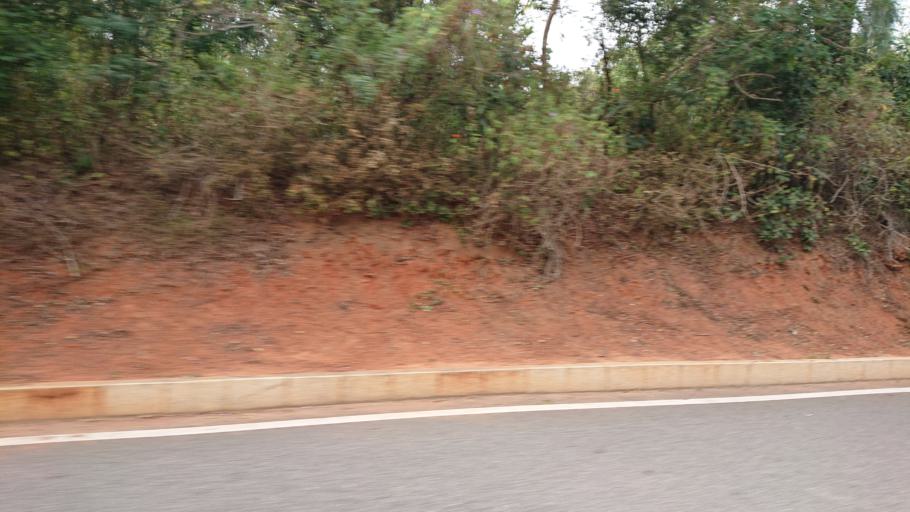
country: TW
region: Fukien
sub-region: Kinmen
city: Jincheng
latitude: 24.4378
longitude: 118.2490
